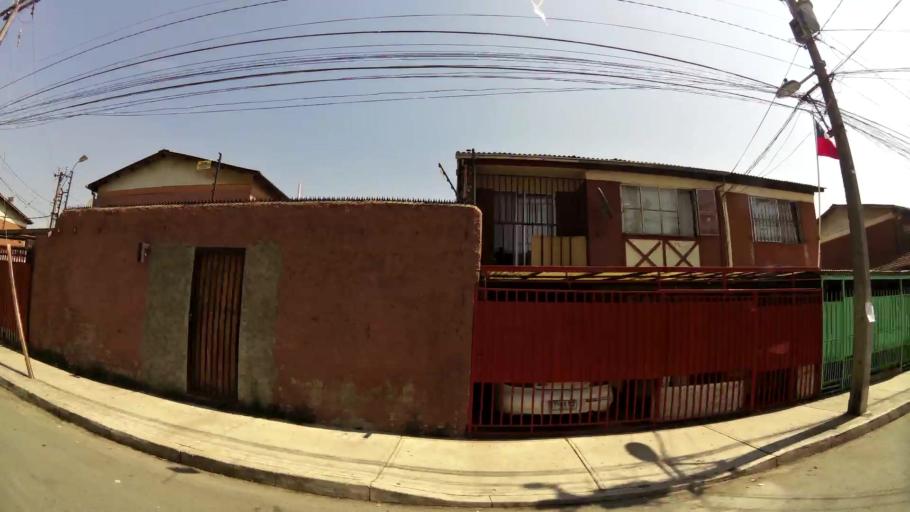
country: CL
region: Santiago Metropolitan
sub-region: Provincia de Santiago
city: La Pintana
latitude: -33.5474
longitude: -70.6162
